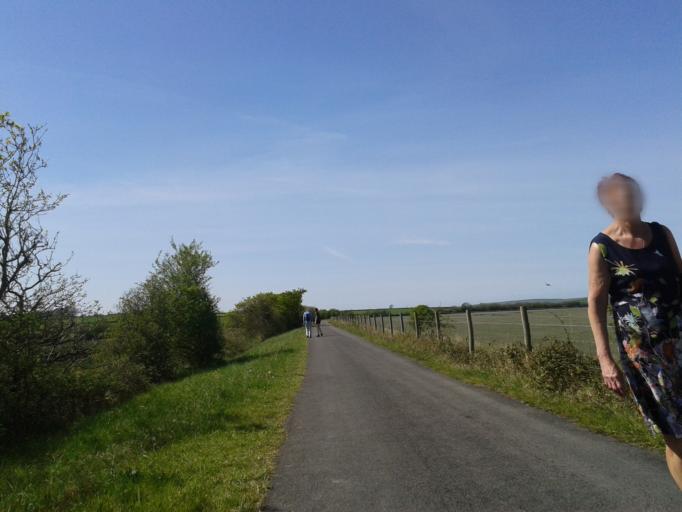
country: GB
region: England
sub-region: Devon
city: Fremington
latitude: 51.0805
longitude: -4.0988
